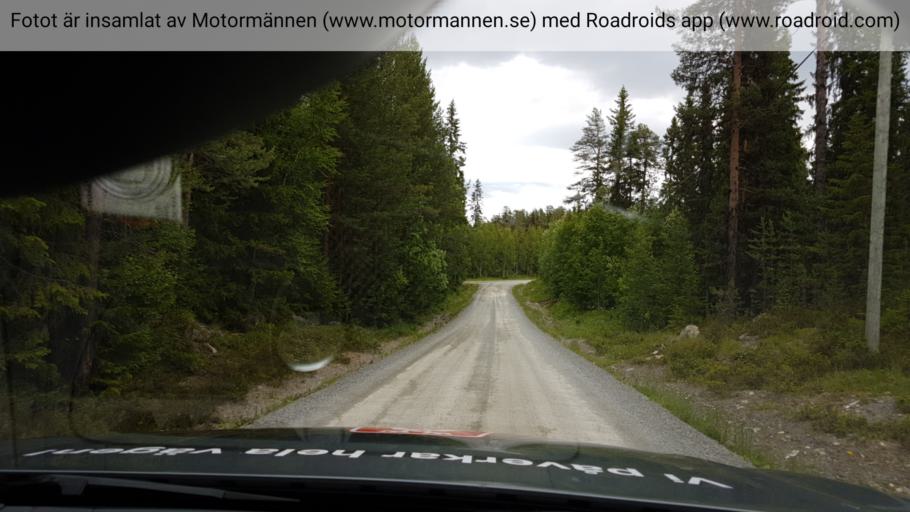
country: SE
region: Jaemtland
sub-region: Bergs Kommun
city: Hoverberg
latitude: 62.7920
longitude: 13.8165
